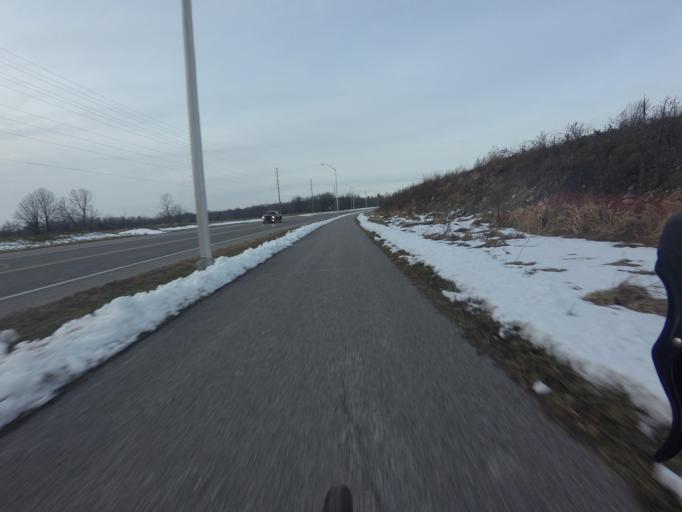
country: CA
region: Ontario
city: Bells Corners
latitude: 45.3214
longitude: -75.9488
